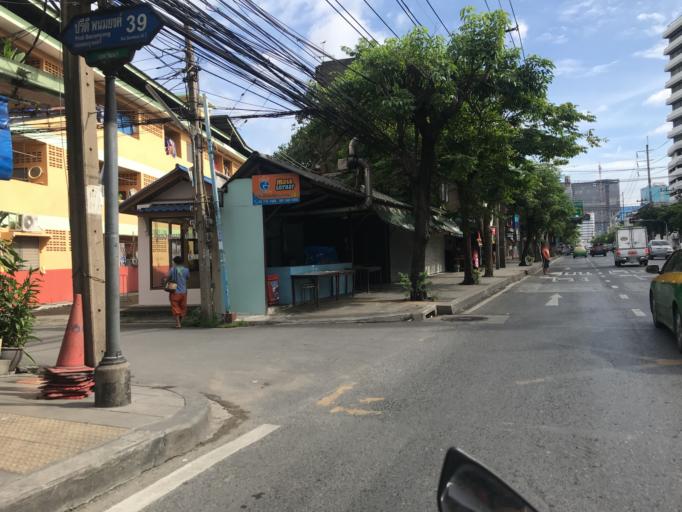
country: TH
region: Bangkok
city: Watthana
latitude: 13.7324
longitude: 100.5970
